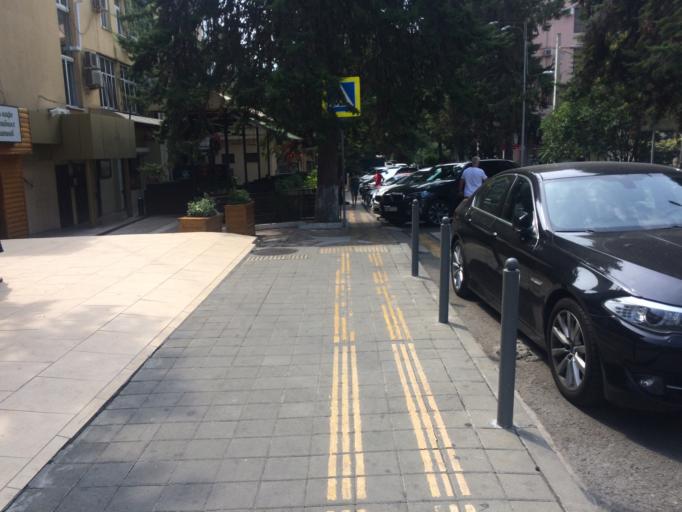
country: RU
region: Krasnodarskiy
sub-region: Sochi City
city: Sochi
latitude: 43.5902
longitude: 39.7246
